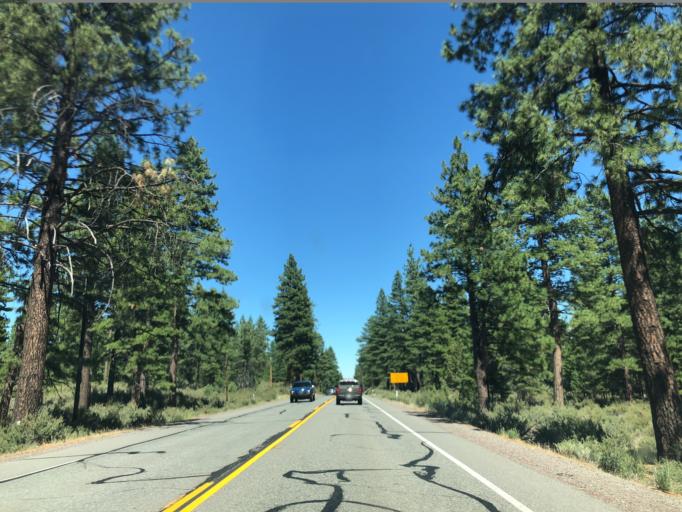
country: US
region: California
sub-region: Lassen County
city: Susanville
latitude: 40.4169
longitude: -120.7169
